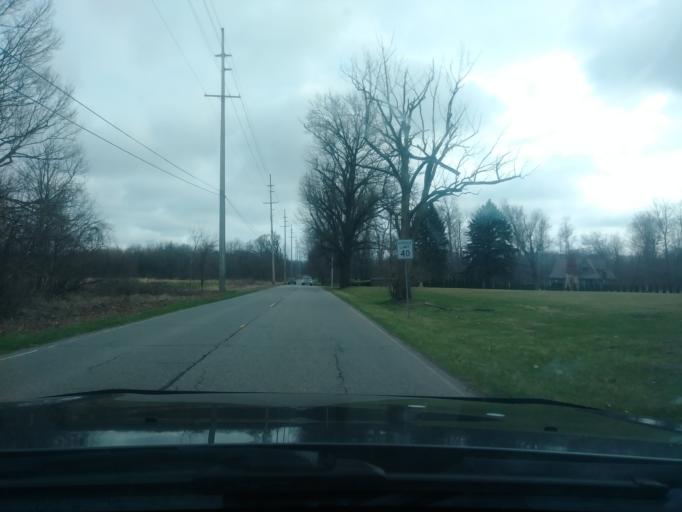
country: US
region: Indiana
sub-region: LaPorte County
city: LaPorte
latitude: 41.6350
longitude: -86.7971
